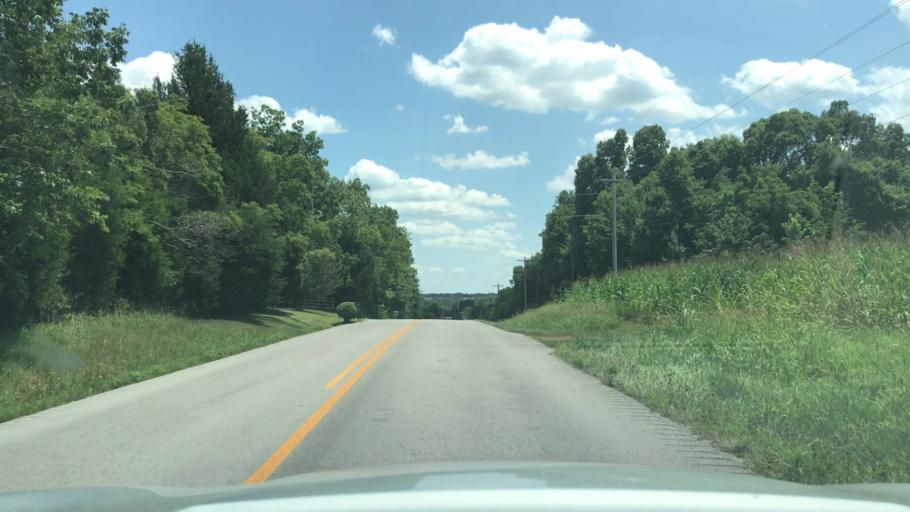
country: US
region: Kentucky
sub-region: Christian County
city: Hopkinsville
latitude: 36.9914
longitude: -87.3621
